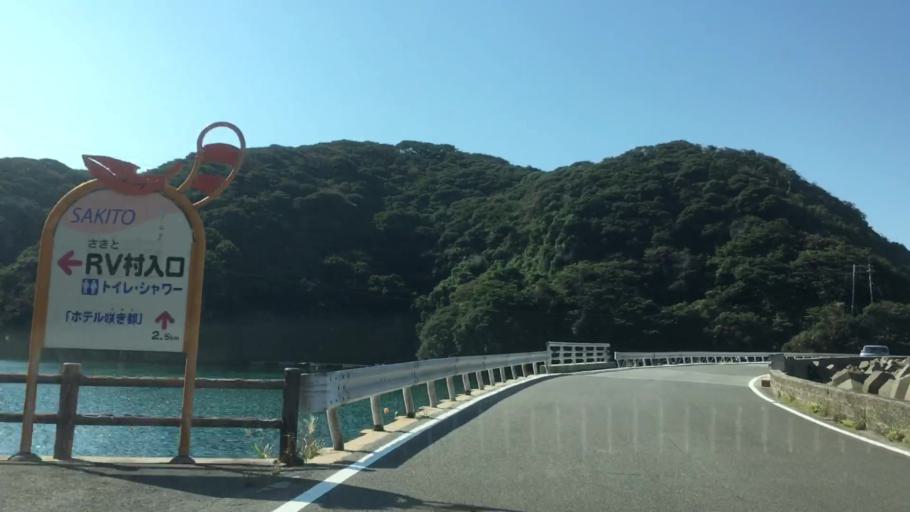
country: JP
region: Nagasaki
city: Sasebo
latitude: 33.0066
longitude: 129.5570
